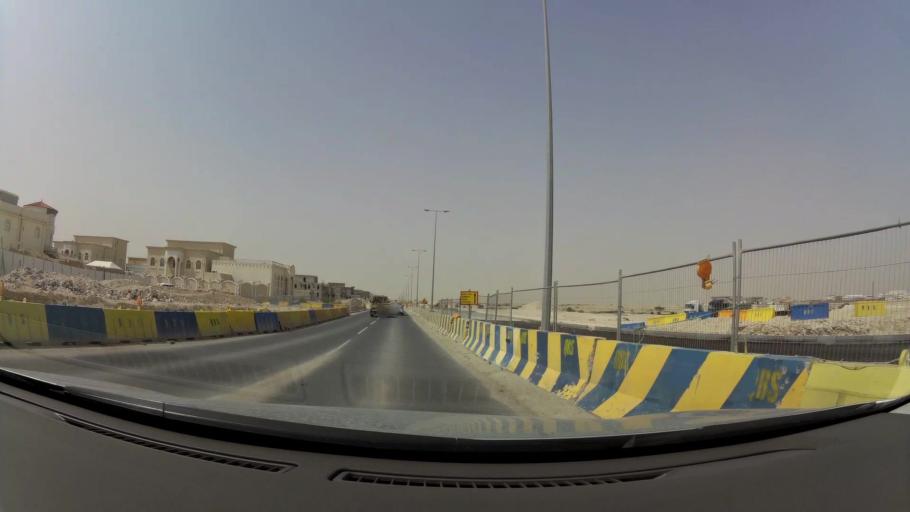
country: QA
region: Baladiyat ar Rayyan
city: Ar Rayyan
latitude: 25.2575
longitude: 51.3770
